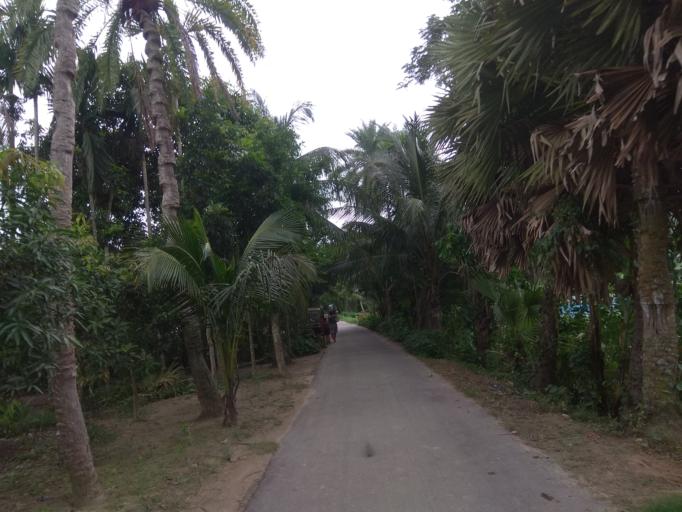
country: BD
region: Dhaka
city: Dohar
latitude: 23.4849
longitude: 89.9999
